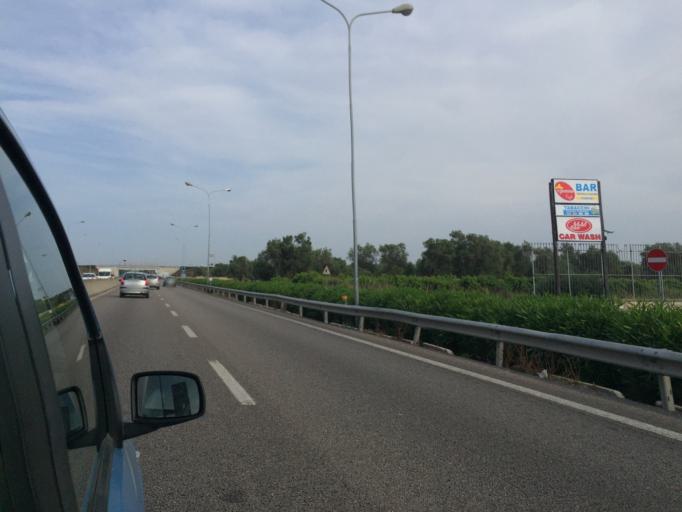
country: IT
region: Apulia
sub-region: Provincia di Bari
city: Triggiano
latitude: 41.0977
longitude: 16.9380
